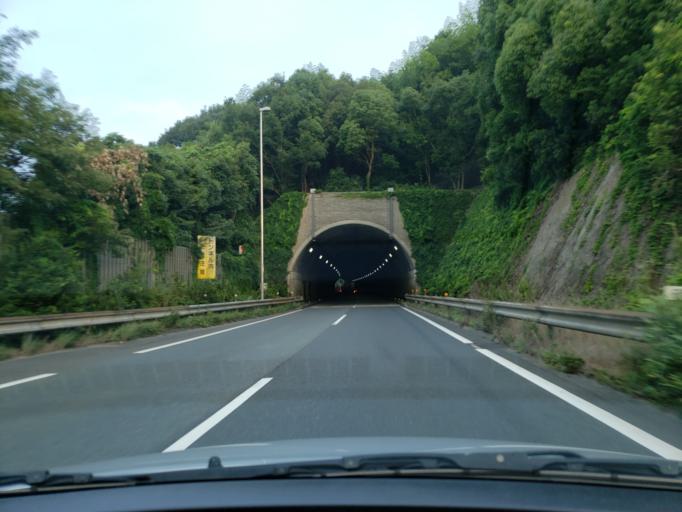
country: JP
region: Hyogo
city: Tatsunocho-tominaga
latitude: 34.8475
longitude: 134.5978
